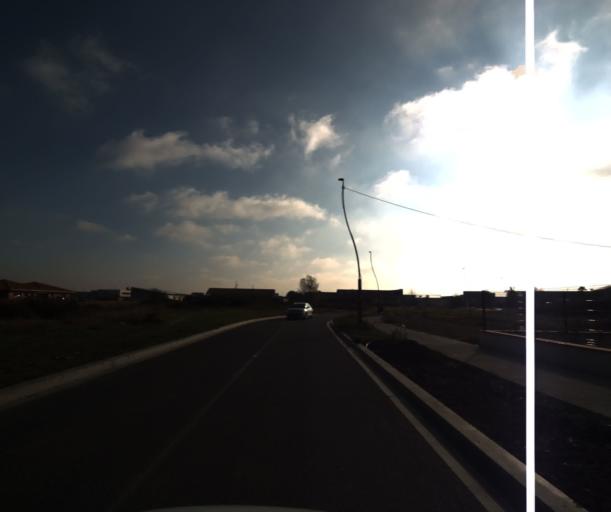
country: FR
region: Midi-Pyrenees
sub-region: Departement de la Haute-Garonne
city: Colomiers
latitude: 43.5954
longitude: 1.3506
